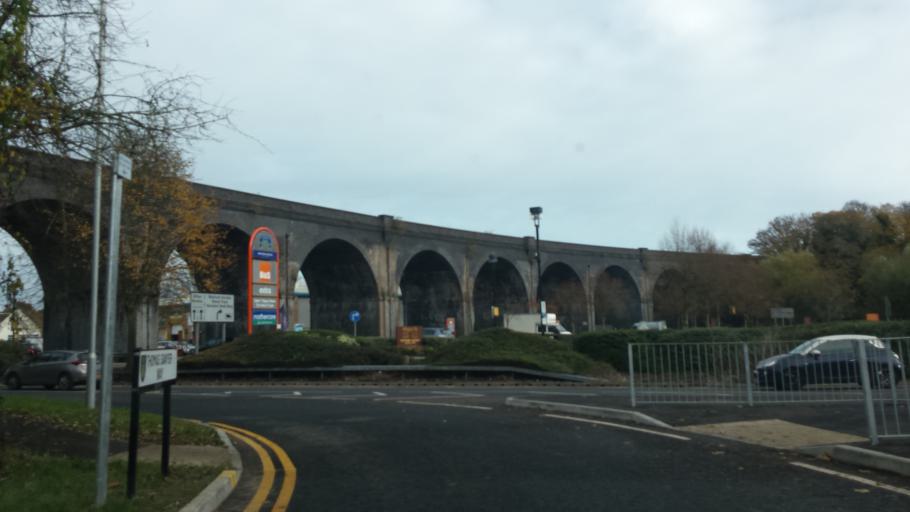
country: GB
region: England
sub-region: Hertfordshire
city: Watford
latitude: 51.6471
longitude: -0.3891
